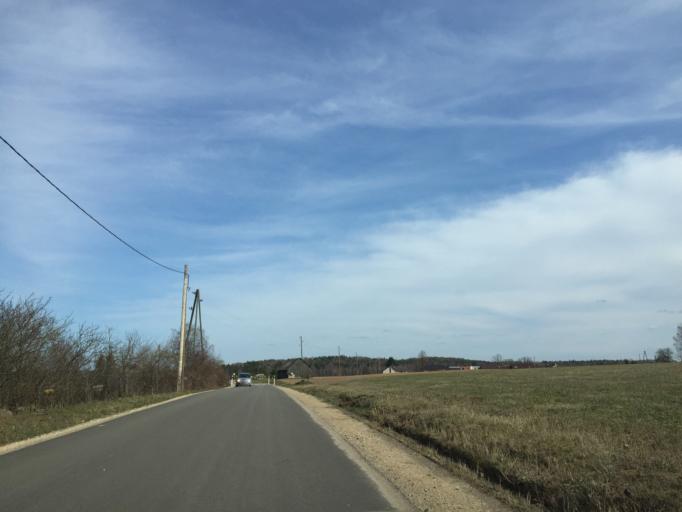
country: LV
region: Ikskile
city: Ikskile
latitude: 56.8404
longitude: 24.5142
